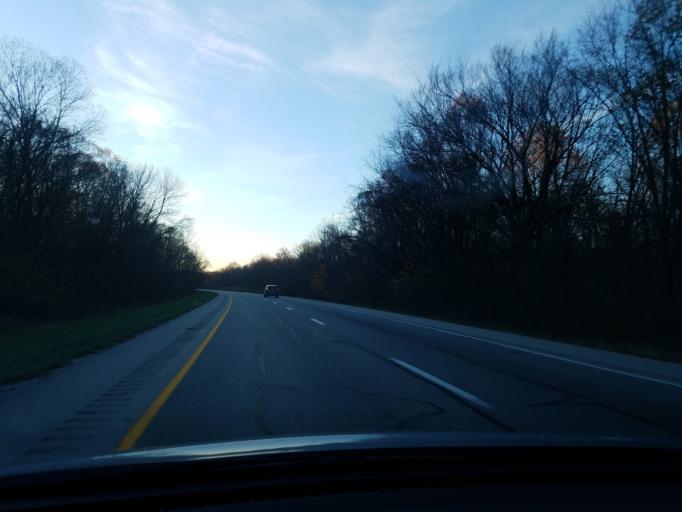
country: US
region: Indiana
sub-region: Posey County
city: Poseyville
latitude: 38.1953
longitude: -87.8453
